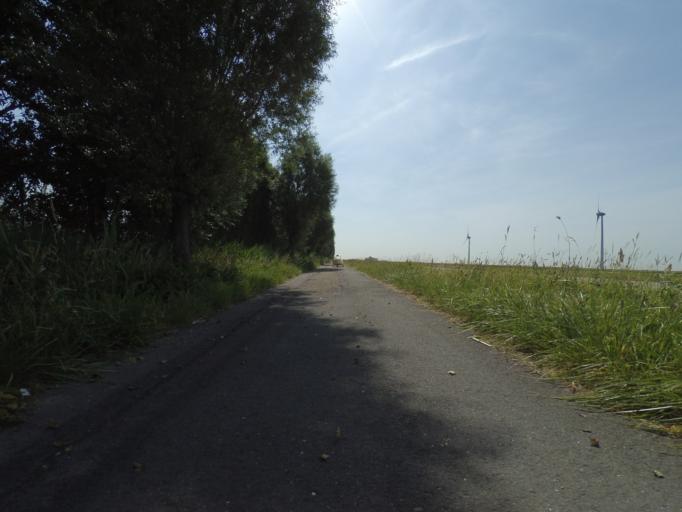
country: NL
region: Zeeland
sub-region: Schouwen-Duiveland
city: Bruinisse
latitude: 51.6370
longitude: 4.1157
